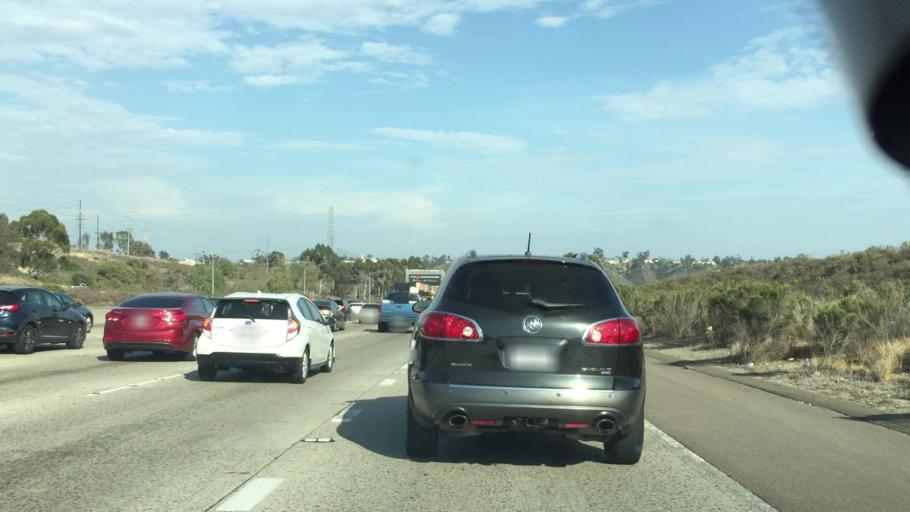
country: US
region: California
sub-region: San Diego County
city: San Diego
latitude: 32.7833
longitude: -117.1423
